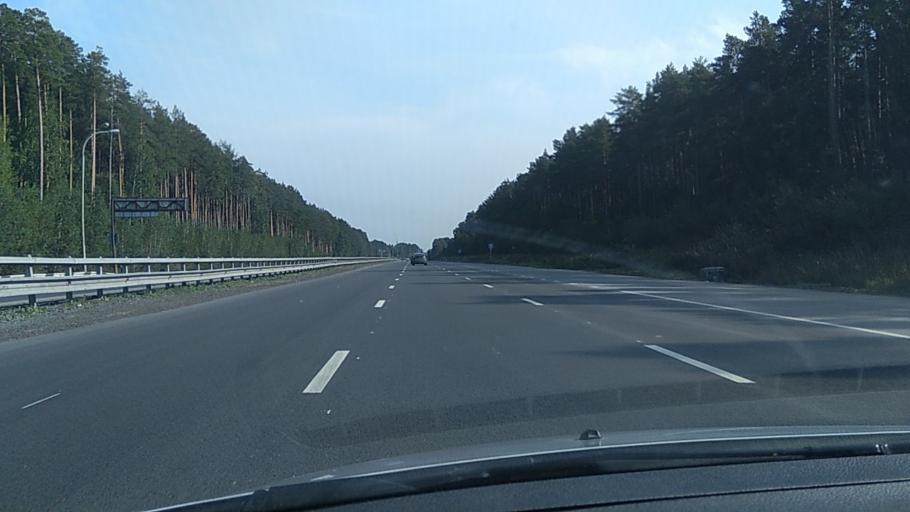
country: RU
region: Sverdlovsk
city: Shuvakish
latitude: 56.8928
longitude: 60.5357
